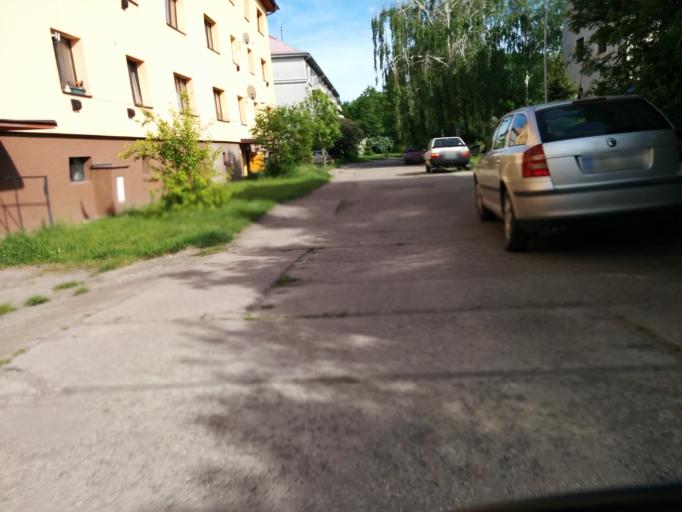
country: CZ
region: Central Bohemia
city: Libis
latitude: 50.2767
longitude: 14.5070
